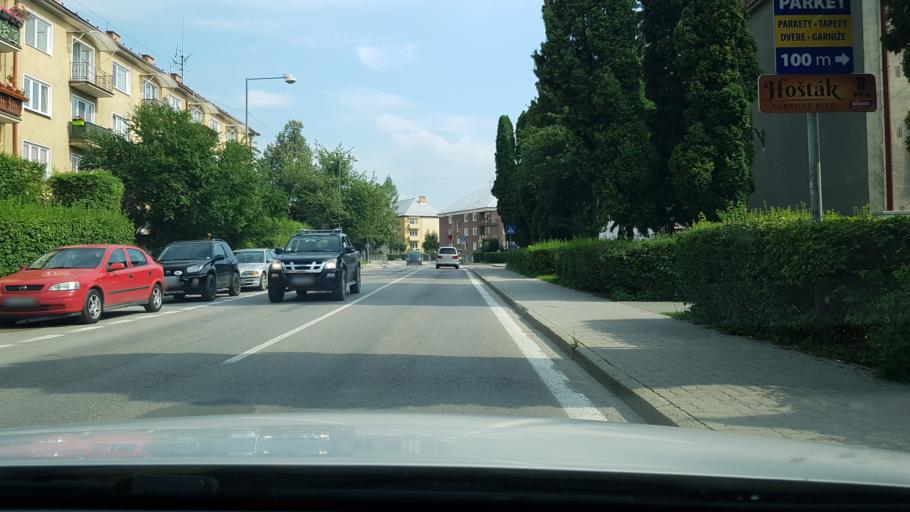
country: SK
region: Trenciansky
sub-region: Okres Povazska Bystrica
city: Povazska Bystrica
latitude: 49.1106
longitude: 18.4548
